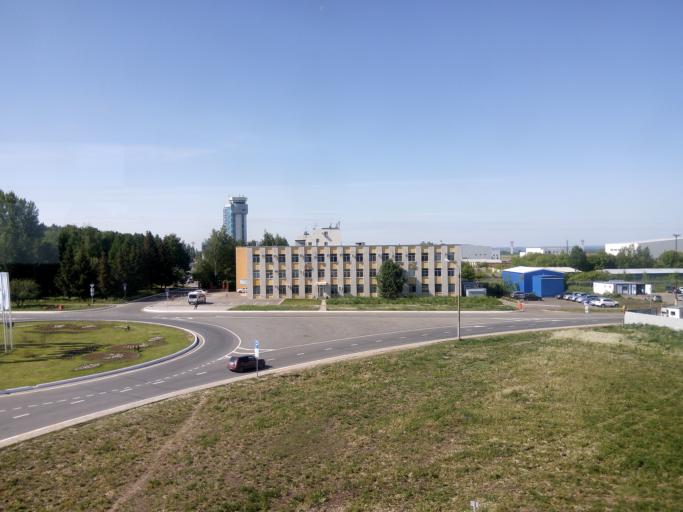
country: RU
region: Tatarstan
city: Stolbishchi
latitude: 55.6147
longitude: 49.2854
